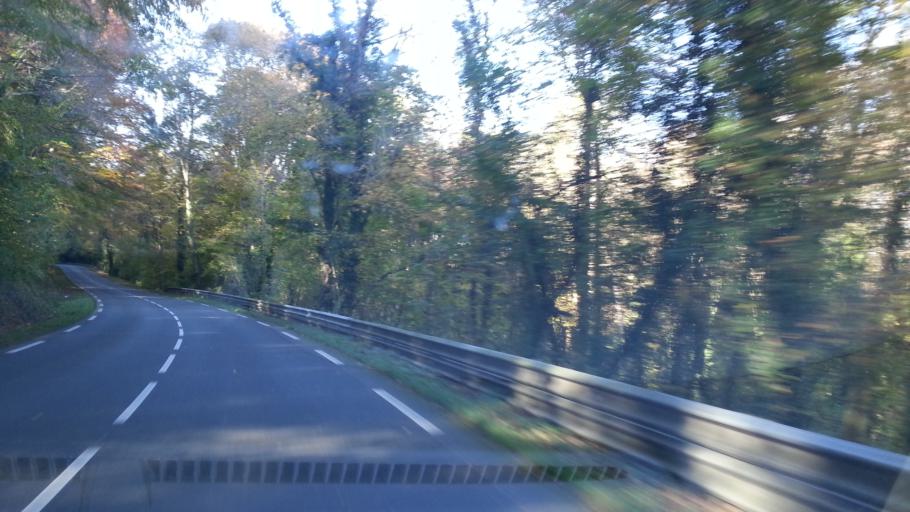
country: FR
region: Picardie
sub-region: Departement de l'Oise
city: Cires-les-Mello
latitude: 49.2858
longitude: 2.3589
